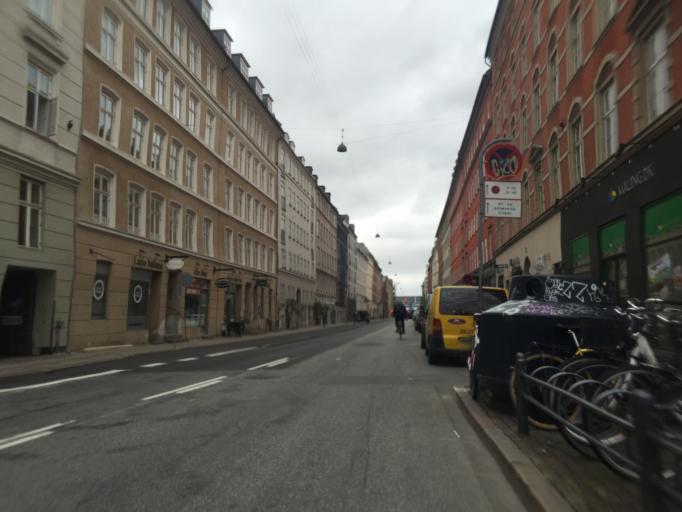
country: DK
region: Capital Region
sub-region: Kobenhavn
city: Copenhagen
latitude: 55.6721
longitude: 12.5557
